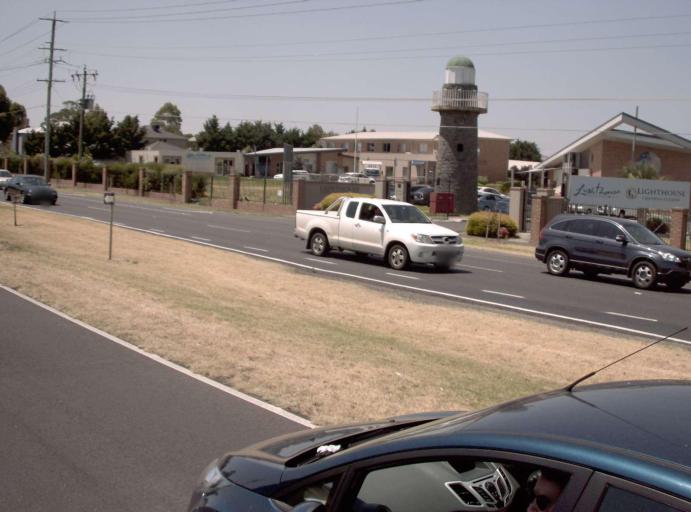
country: AU
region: Victoria
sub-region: Kingston
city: Waterways
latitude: -38.0014
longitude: 145.1425
